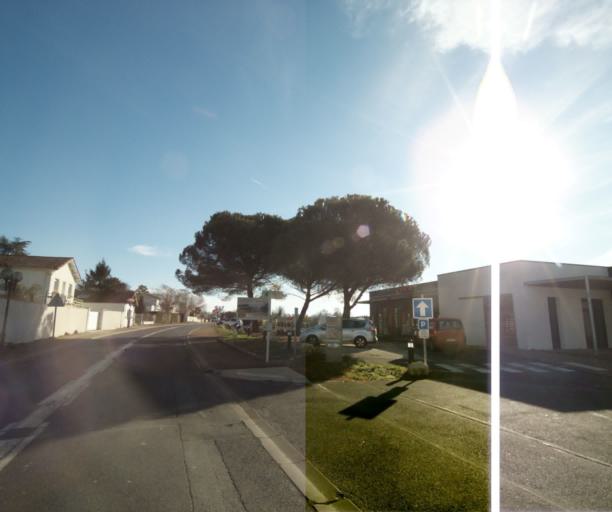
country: FR
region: Poitou-Charentes
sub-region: Departement de la Charente-Maritime
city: Chaniers
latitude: 45.7177
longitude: -0.5560
